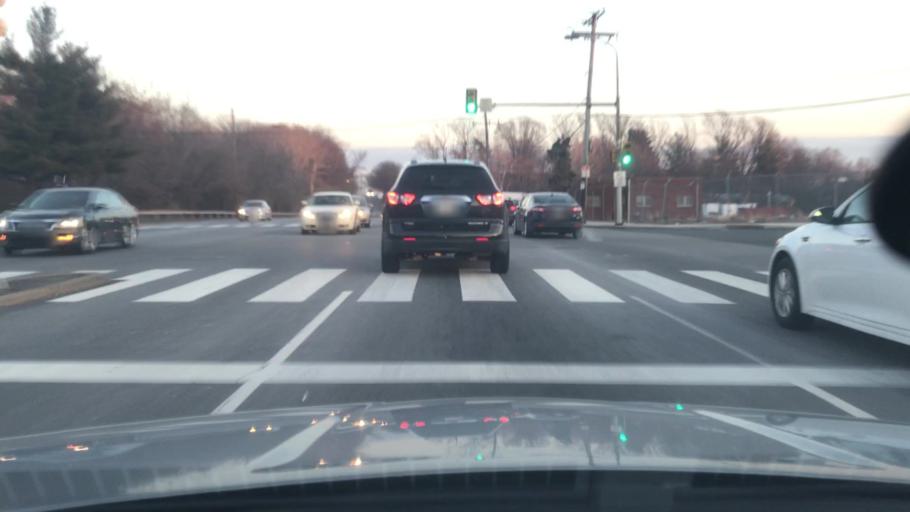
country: US
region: New Jersey
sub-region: Burlington County
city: Riverton
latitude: 40.0722
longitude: -75.0134
